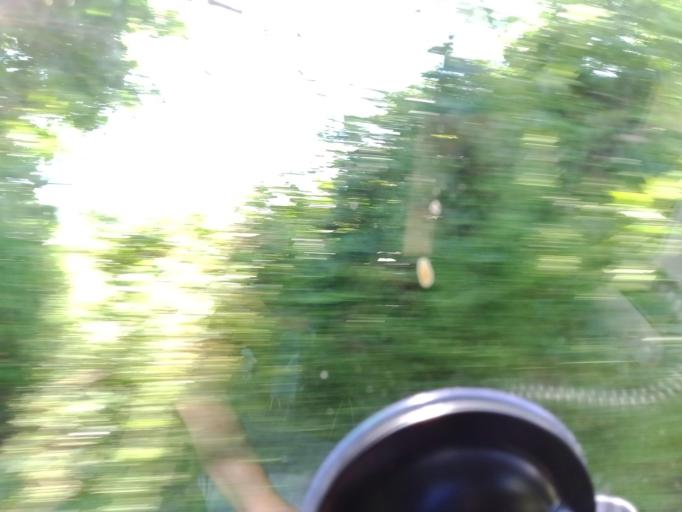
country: IE
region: Leinster
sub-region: Kilkenny
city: Thomastown
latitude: 52.5545
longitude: -7.0980
